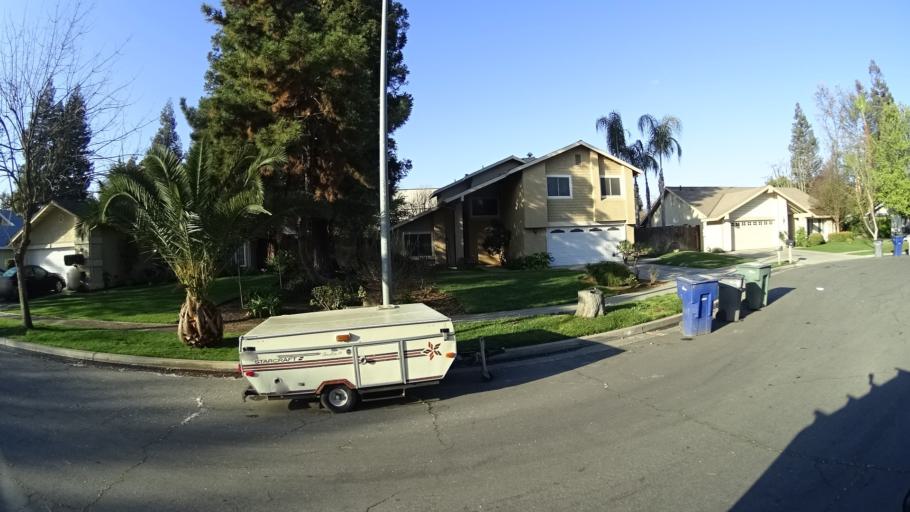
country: US
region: California
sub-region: Fresno County
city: West Park
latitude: 36.8144
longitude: -119.8667
